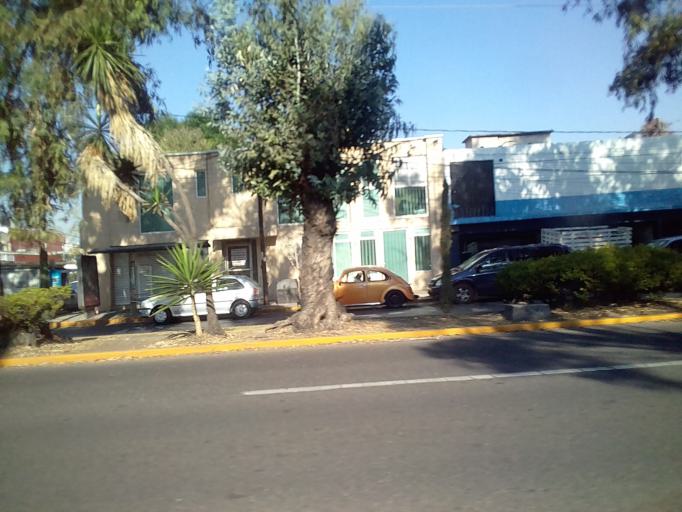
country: MX
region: Mexico
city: Naucalpan de Juarez
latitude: 19.4863
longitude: -99.2295
